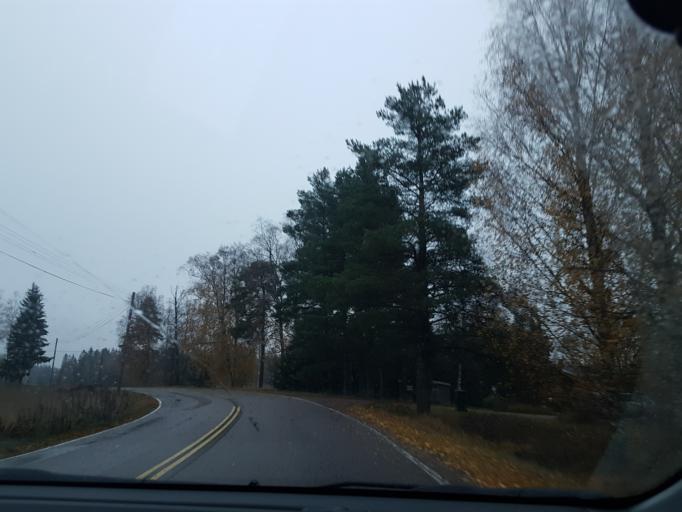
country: FI
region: Uusimaa
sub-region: Helsinki
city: Maentsaelae
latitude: 60.6030
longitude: 25.2045
